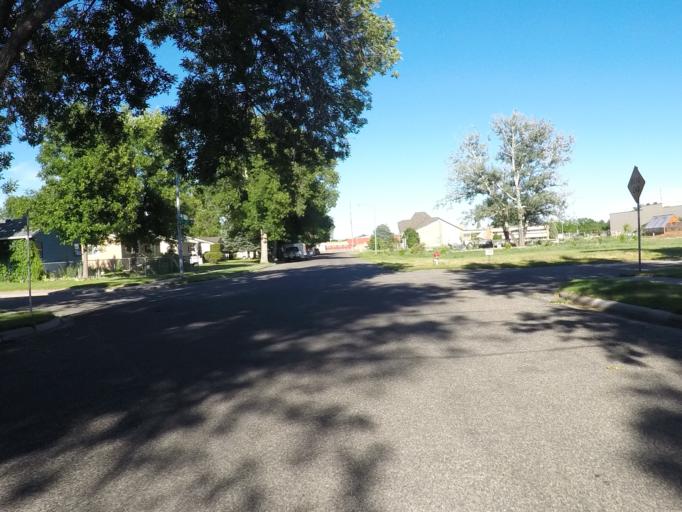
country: US
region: Montana
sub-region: Yellowstone County
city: Billings
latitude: 45.7728
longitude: -108.5792
